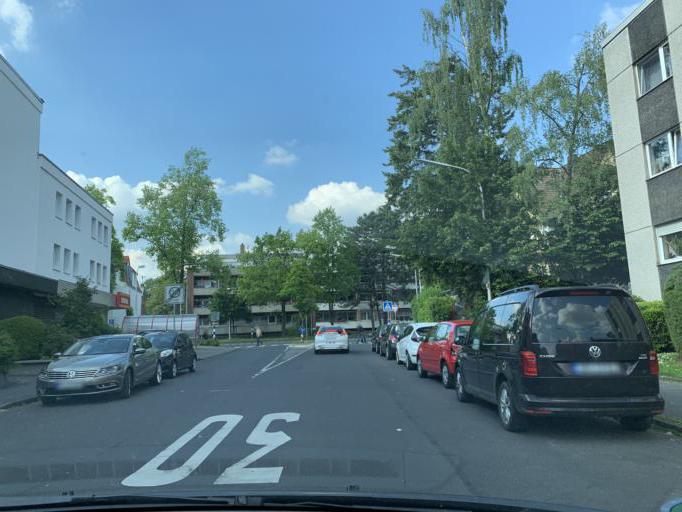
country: DE
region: North Rhine-Westphalia
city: Bruhl
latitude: 50.8340
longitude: 6.9000
